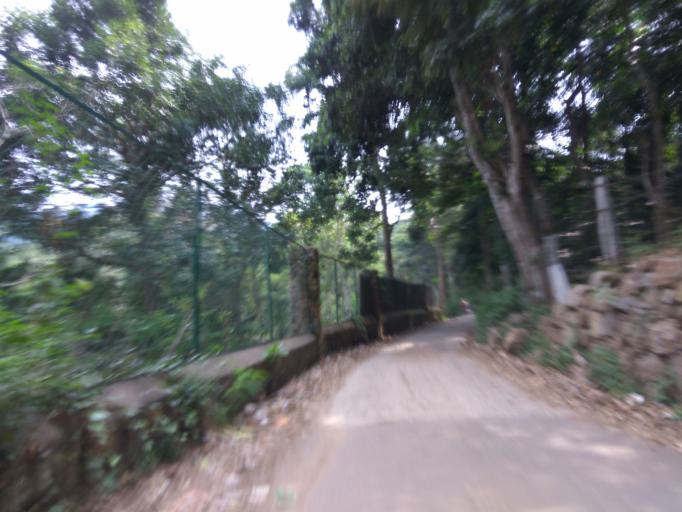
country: IN
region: Tamil Nadu
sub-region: Salem
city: Salem
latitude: 11.7935
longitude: 78.2018
